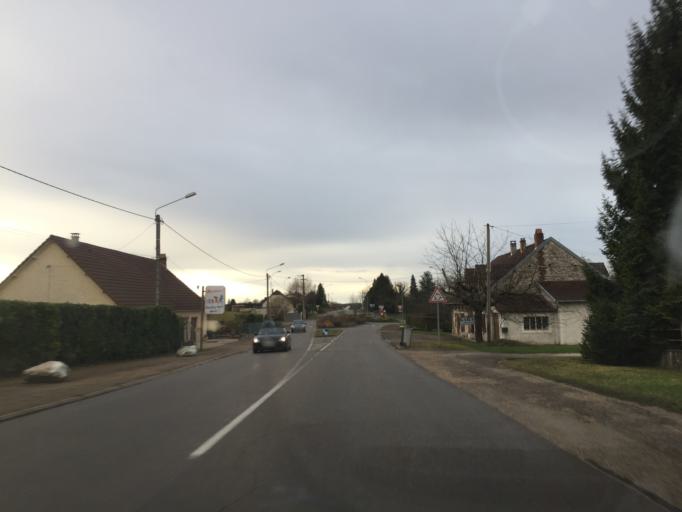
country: FR
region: Franche-Comte
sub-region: Departement du Jura
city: Choisey
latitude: 47.0537
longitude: 5.4940
